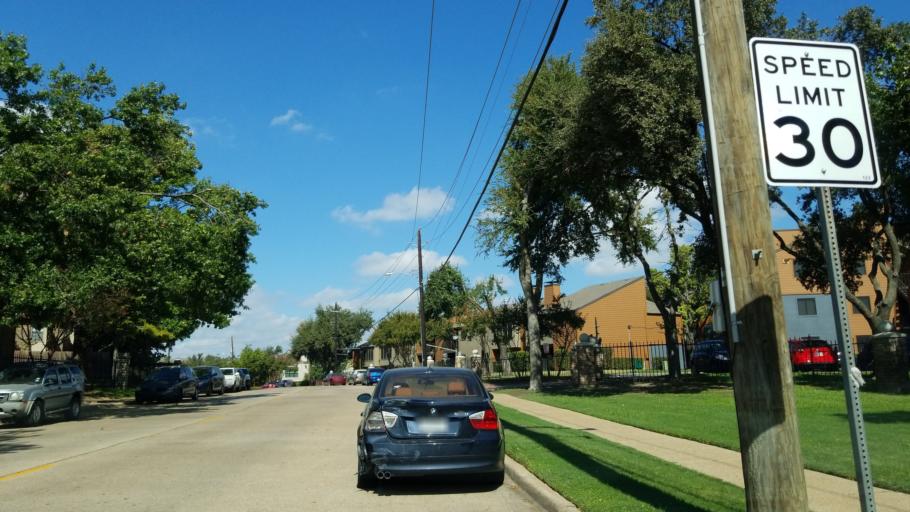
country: US
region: Texas
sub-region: Dallas County
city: Addison
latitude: 32.9426
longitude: -96.8088
